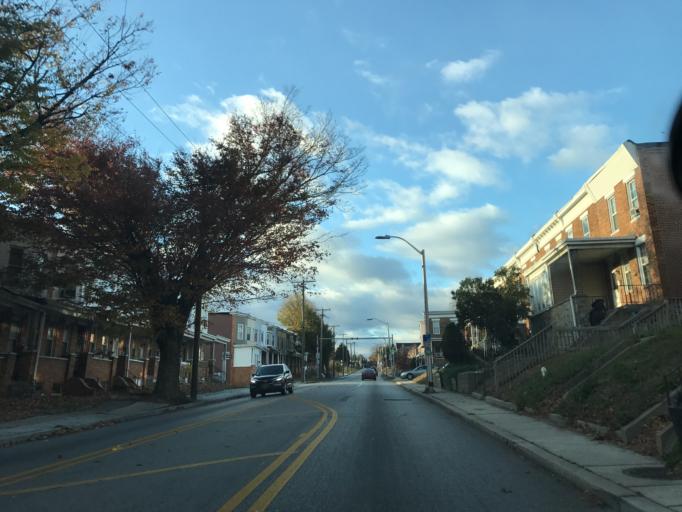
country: US
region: Maryland
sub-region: City of Baltimore
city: Baltimore
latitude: 39.3224
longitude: -76.5748
